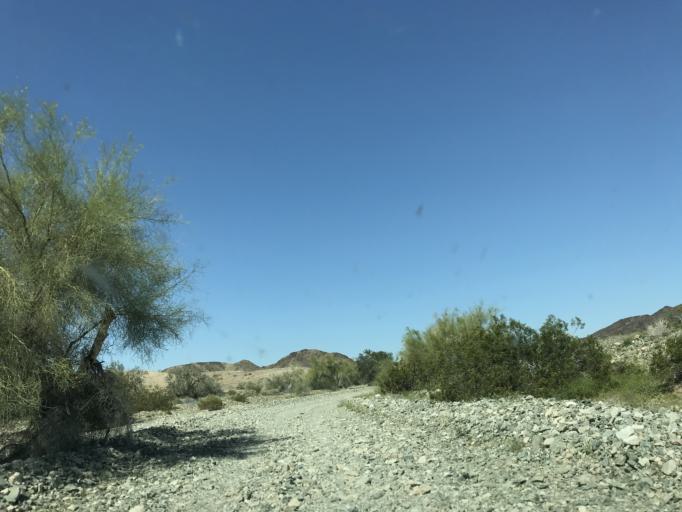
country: US
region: California
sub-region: Riverside County
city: Mesa Verde
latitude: 33.4933
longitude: -114.8261
